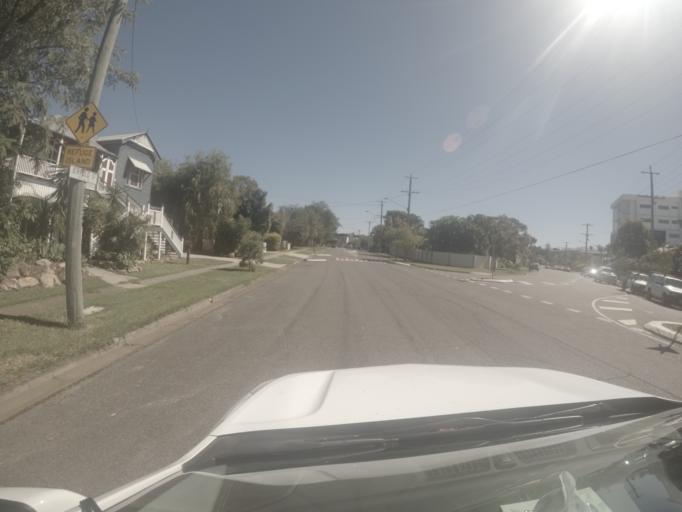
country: AU
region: Queensland
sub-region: Brisbane
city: Rocklea
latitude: -27.5347
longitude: 152.9854
